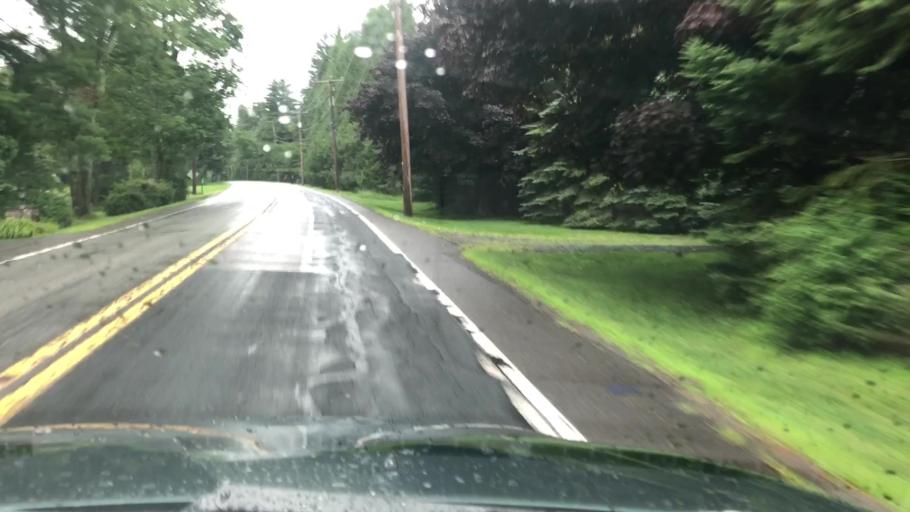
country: US
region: Pennsylvania
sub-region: Monroe County
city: Mountainhome
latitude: 41.2193
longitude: -75.2342
